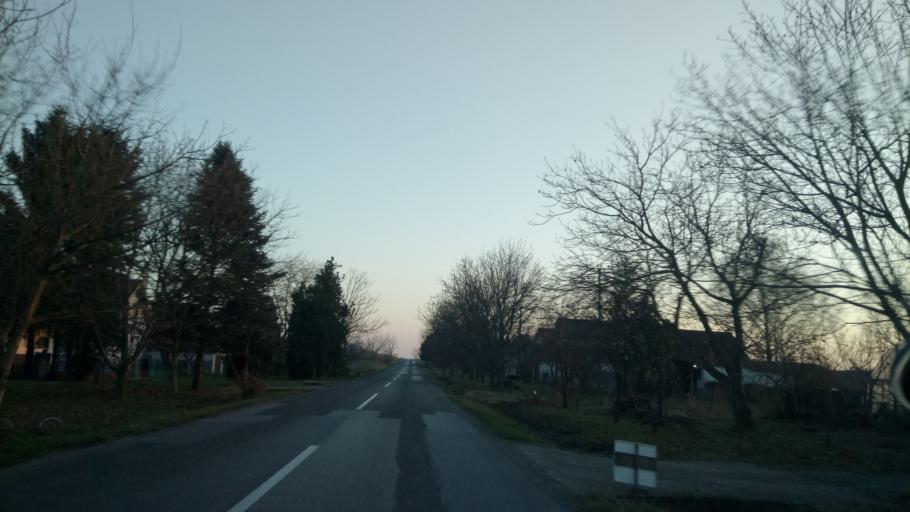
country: RS
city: Surduk
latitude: 45.0645
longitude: 20.3301
